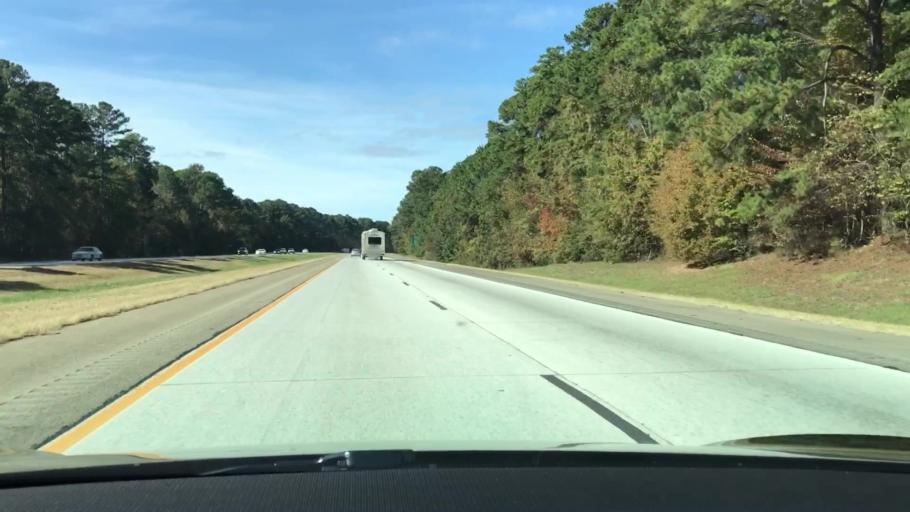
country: US
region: Georgia
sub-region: Putnam County
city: Jefferson
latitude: 33.5332
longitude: -83.2857
